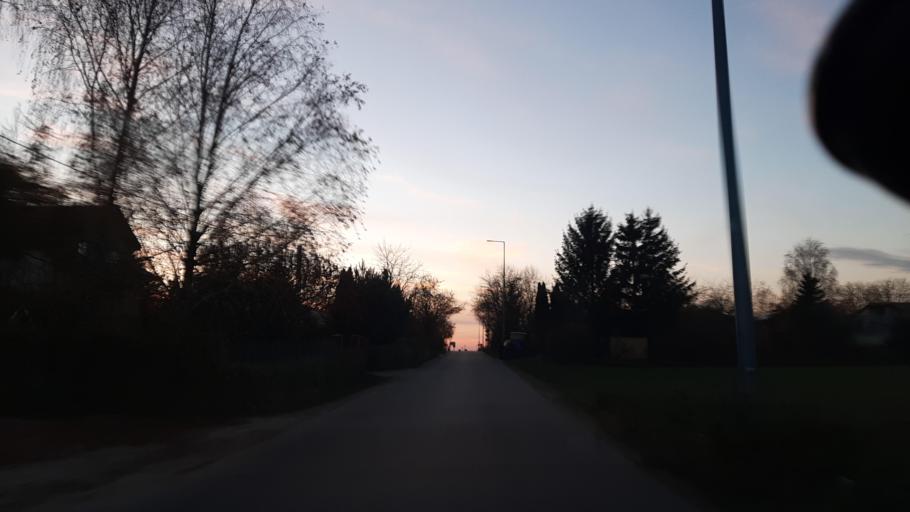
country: PL
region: Lublin Voivodeship
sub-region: Powiat lubelski
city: Jastkow
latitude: 51.3242
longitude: 22.4379
